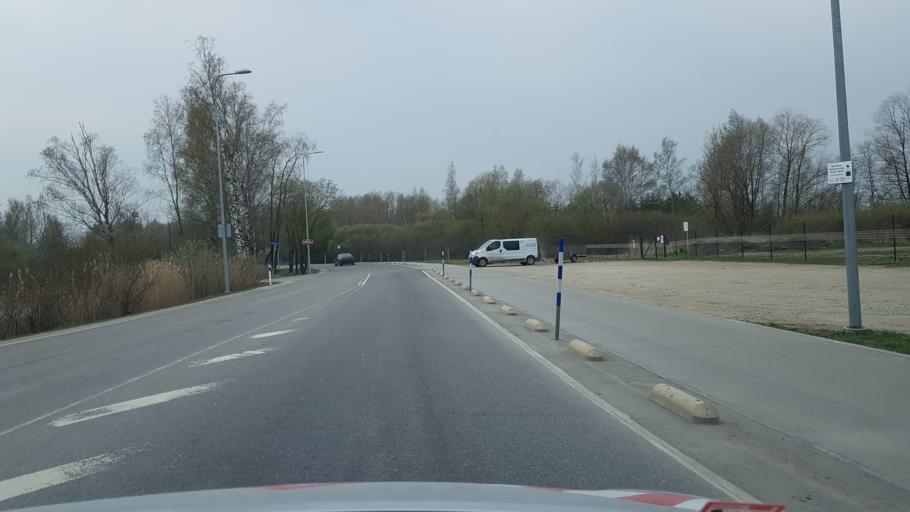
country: EE
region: Harju
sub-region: Tallinna linn
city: Tallinn
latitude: 59.4117
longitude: 24.8010
